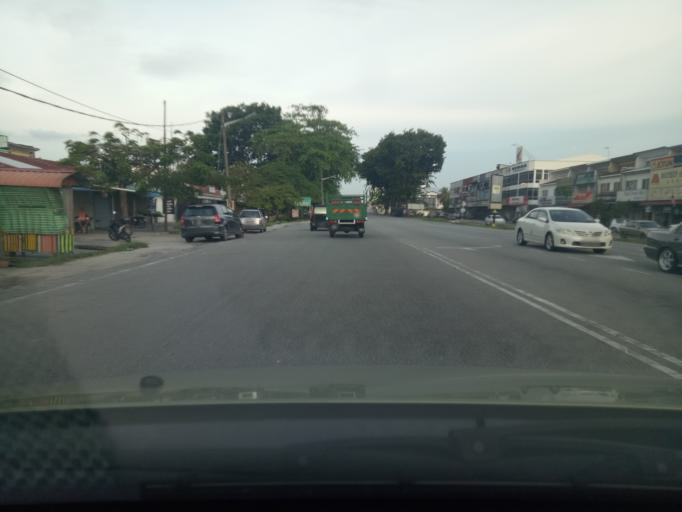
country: MY
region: Kedah
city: Alor Setar
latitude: 6.1250
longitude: 100.3580
